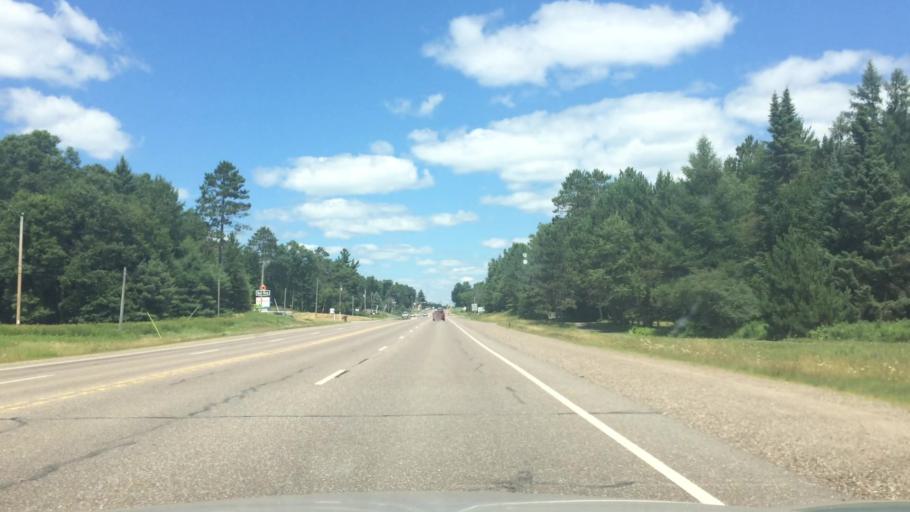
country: US
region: Wisconsin
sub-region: Vilas County
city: Lac du Flambeau
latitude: 45.9145
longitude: -89.6949
